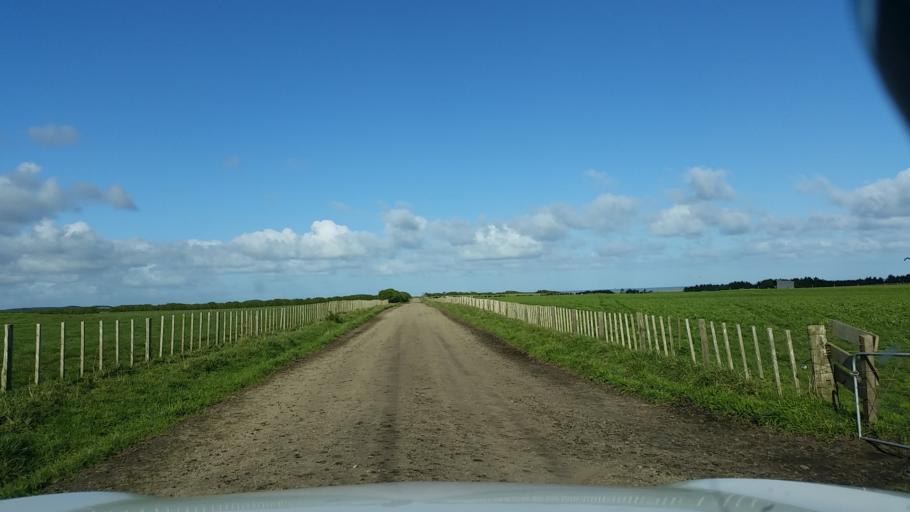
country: NZ
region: Taranaki
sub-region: South Taranaki District
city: Patea
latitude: -39.7504
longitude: 174.5191
